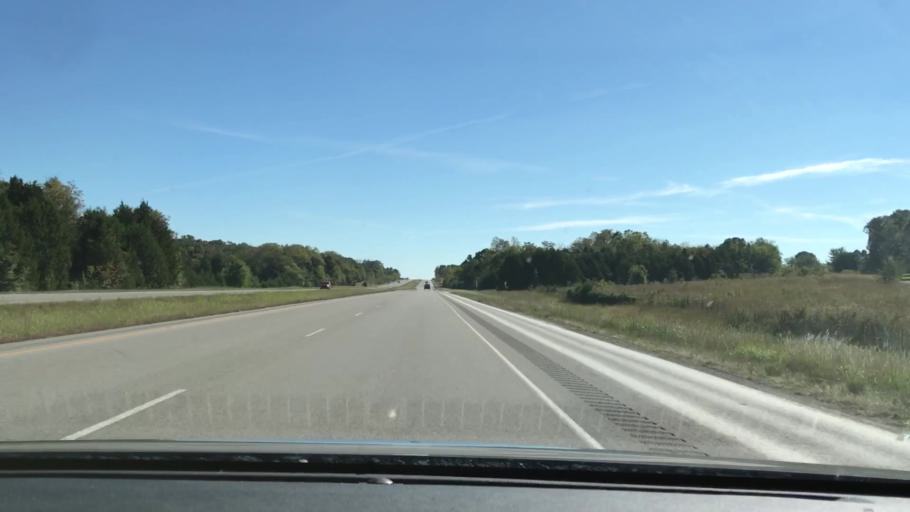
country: US
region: Kentucky
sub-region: Christian County
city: Hopkinsville
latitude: 36.8477
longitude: -87.3269
